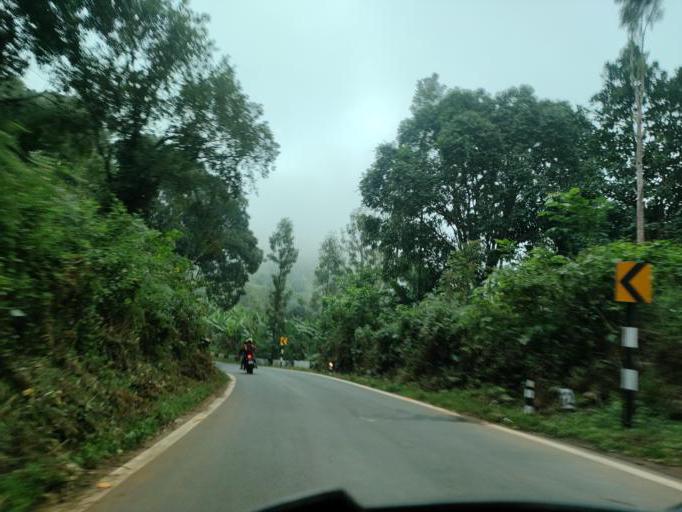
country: IN
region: Tamil Nadu
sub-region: Dindigul
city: Ayakudi
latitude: 10.3377
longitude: 77.5618
